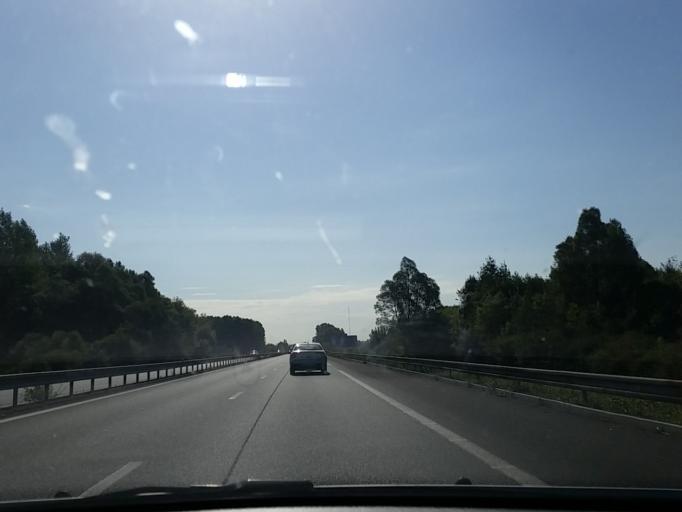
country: FR
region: Centre
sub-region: Departement du Cher
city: Foecy
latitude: 47.2022
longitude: 2.1322
